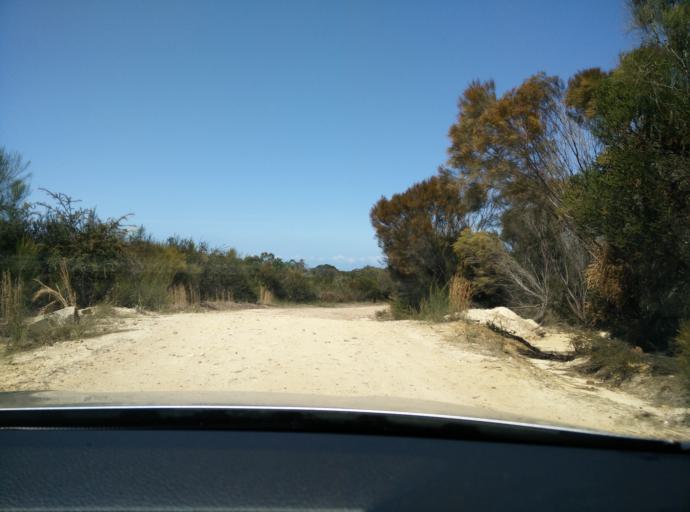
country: AU
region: New South Wales
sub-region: Gosford Shire
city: Umina
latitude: -33.5465
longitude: 151.2857
